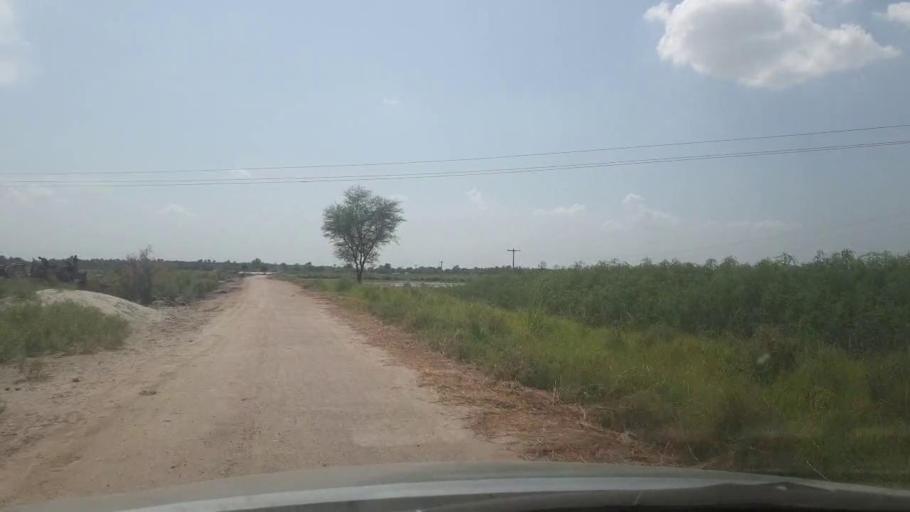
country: PK
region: Sindh
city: Khairpur
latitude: 27.5241
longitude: 68.8049
